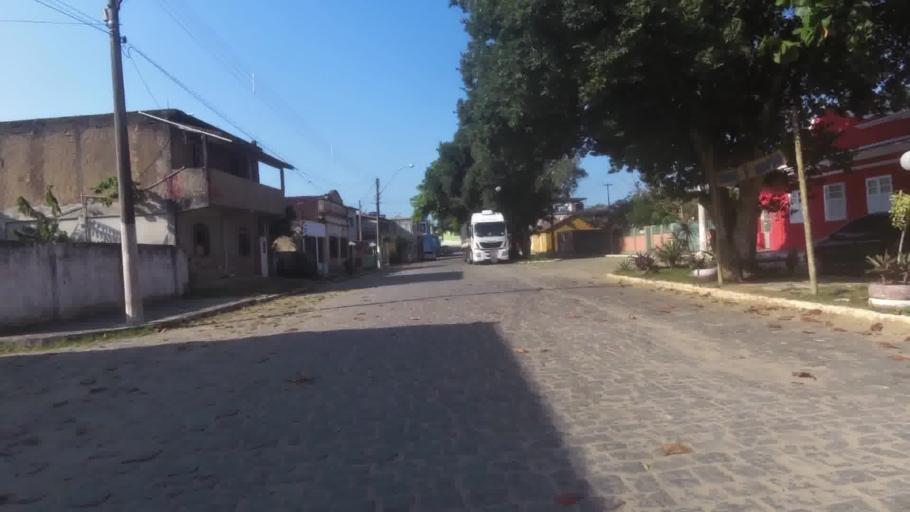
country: BR
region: Espirito Santo
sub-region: Itapemirim
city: Itapemirim
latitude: -21.0084
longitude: -40.8122
